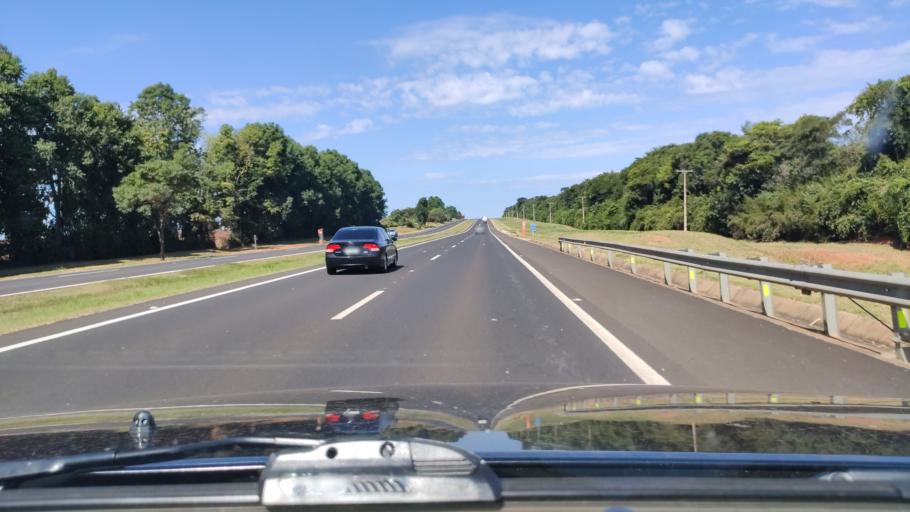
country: BR
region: Sao Paulo
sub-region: Rancharia
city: Rancharia
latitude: -22.4022
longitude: -51.0656
